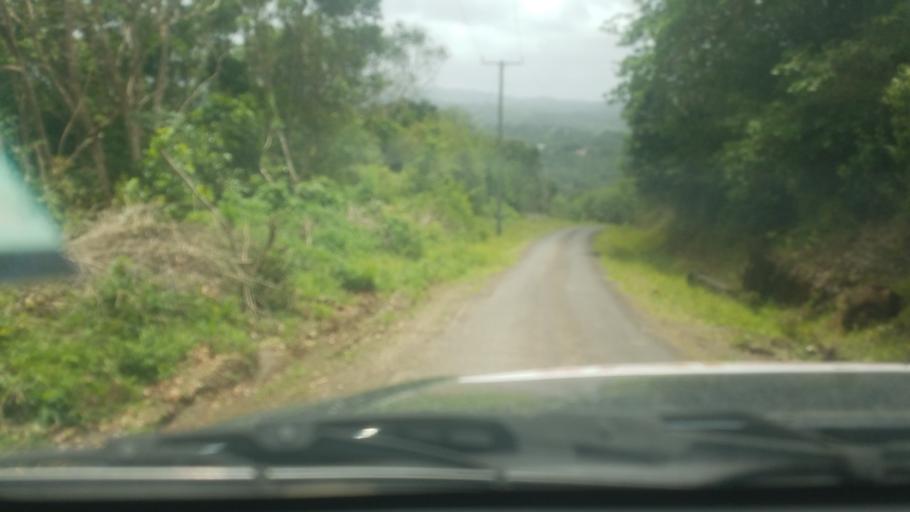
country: LC
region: Laborie Quarter
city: Laborie
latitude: 13.7712
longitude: -61.0031
